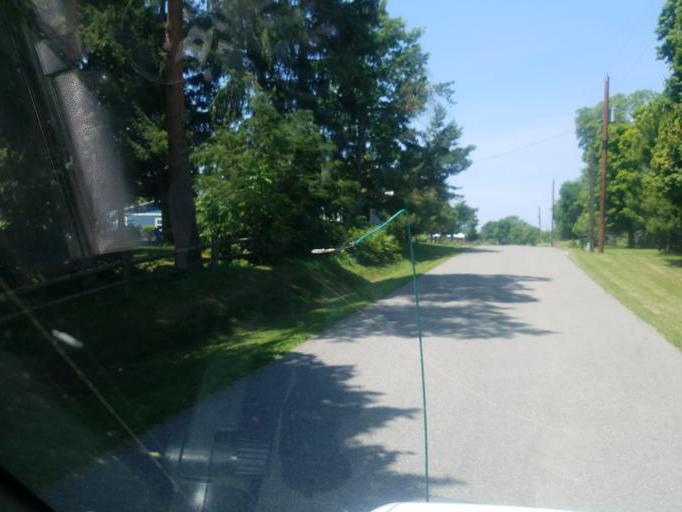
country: US
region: Ohio
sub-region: Logan County
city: West Liberty
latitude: 40.2916
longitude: -83.8208
